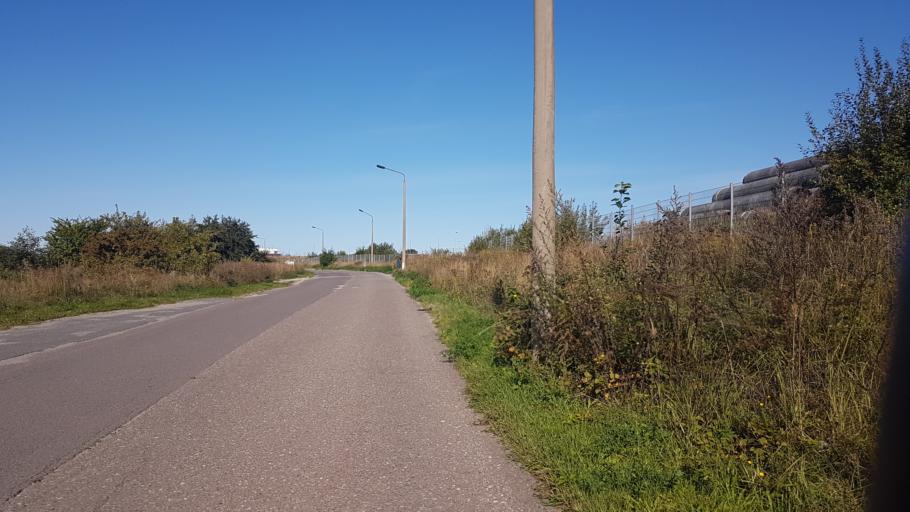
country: DE
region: Mecklenburg-Vorpommern
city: Sagard
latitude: 54.4912
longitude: 13.5703
